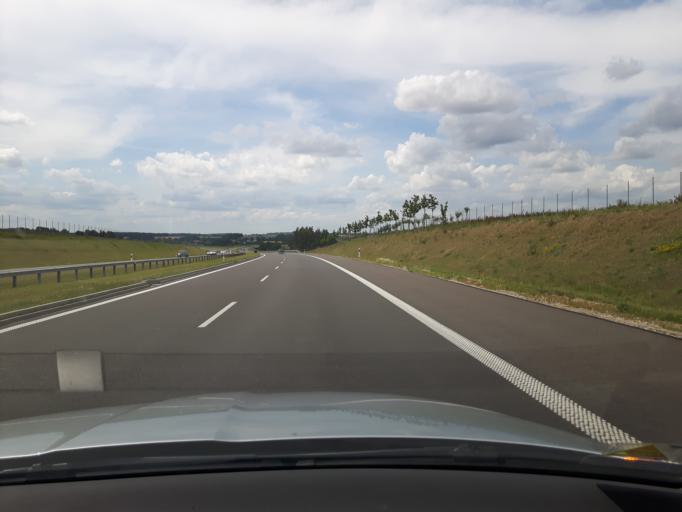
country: PL
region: Warmian-Masurian Voivodeship
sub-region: Powiat nidzicki
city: Nidzica
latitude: 53.3391
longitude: 20.4238
